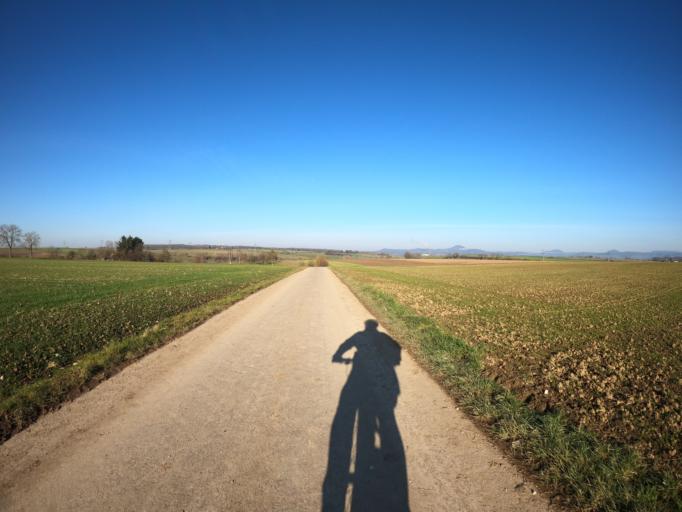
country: DE
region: Baden-Wuerttemberg
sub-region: Regierungsbezirk Stuttgart
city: Heiningen
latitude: 48.6660
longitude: 9.6629
